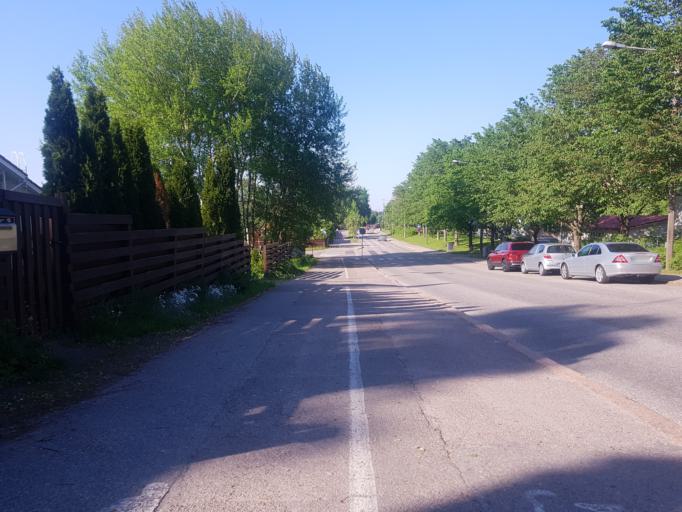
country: FI
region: Uusimaa
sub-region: Helsinki
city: Vantaa
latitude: 60.2635
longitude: 25.0122
